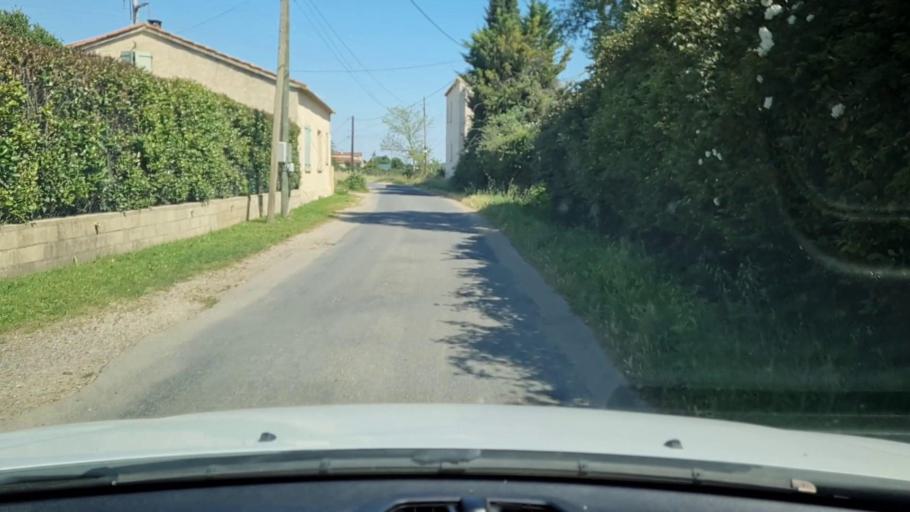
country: FR
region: Languedoc-Roussillon
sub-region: Departement du Gard
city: Le Cailar
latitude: 43.6607
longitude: 4.2340
